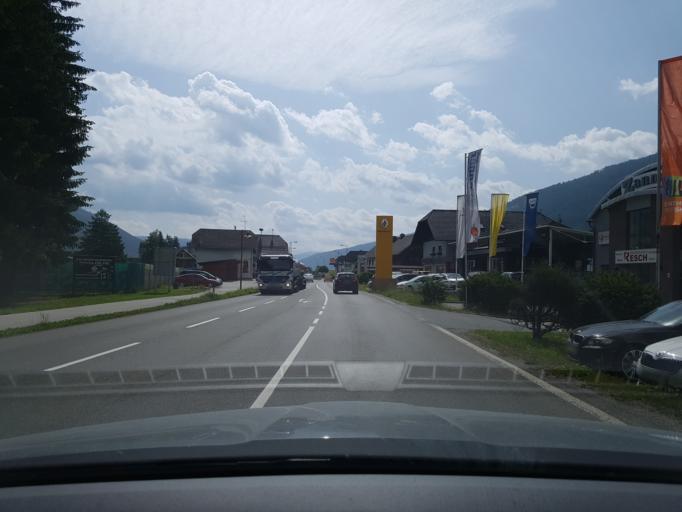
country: AT
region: Salzburg
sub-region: Politischer Bezirk Tamsweg
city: Sankt Michael im Lungau
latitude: 47.0962
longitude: 13.6345
